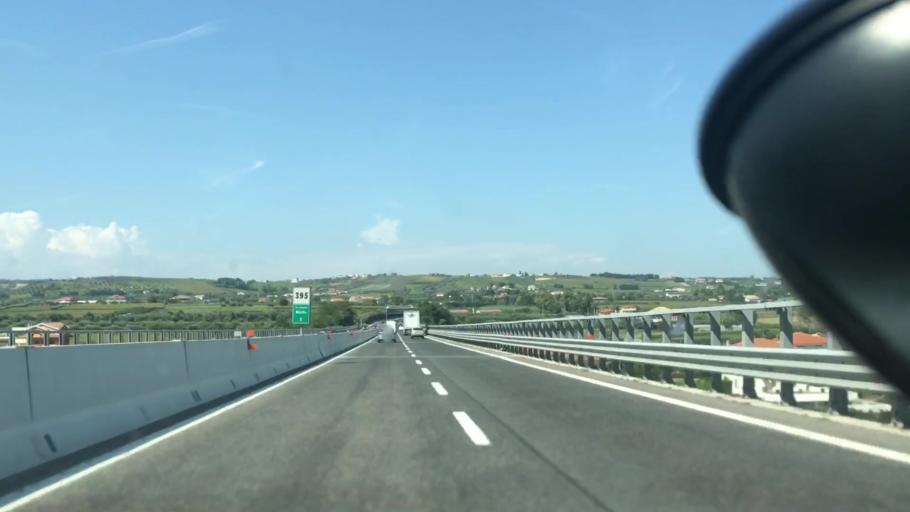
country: IT
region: Abruzzo
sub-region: Provincia di Chieti
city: Miglianico
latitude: 42.3756
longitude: 14.3024
